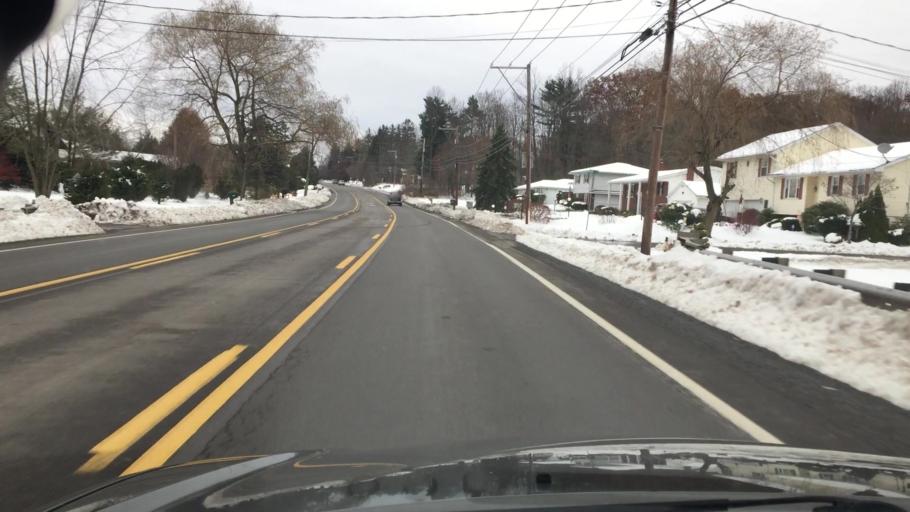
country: US
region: Pennsylvania
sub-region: Luzerne County
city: Mountain Top
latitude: 41.1153
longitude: -75.9131
